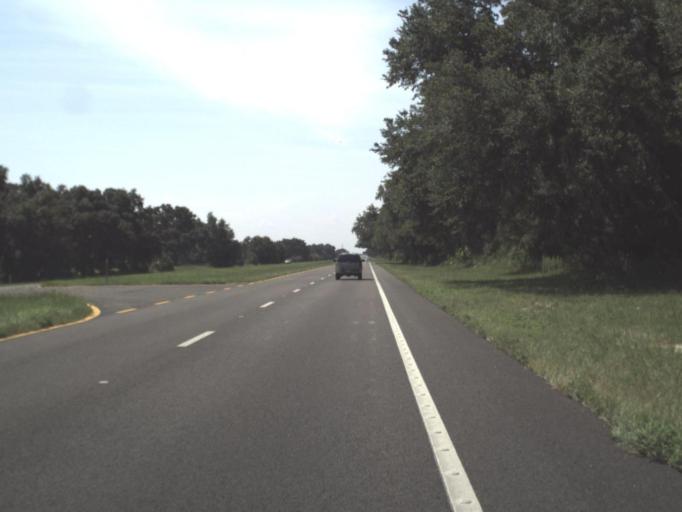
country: US
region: Florida
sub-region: Levy County
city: Inglis
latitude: 28.9800
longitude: -82.6413
